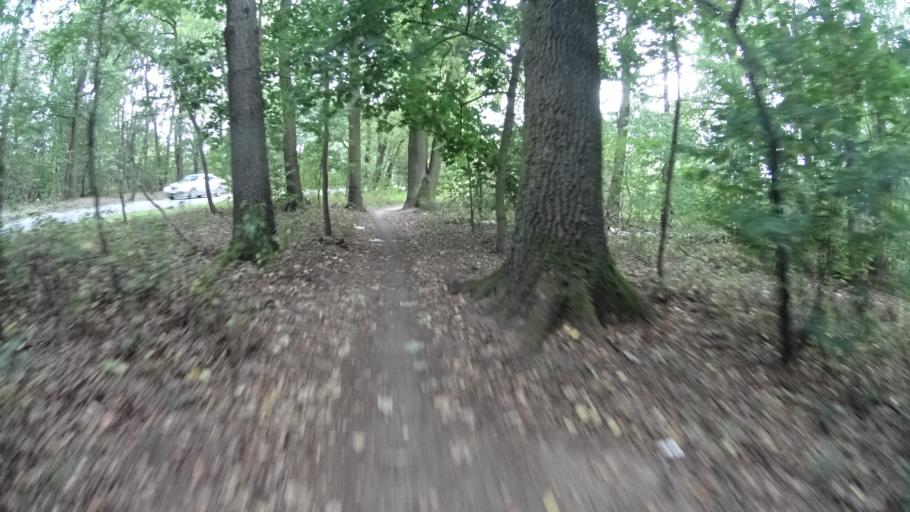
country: PL
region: Masovian Voivodeship
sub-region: Powiat pruszkowski
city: Granica
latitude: 52.1289
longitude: 20.7995
